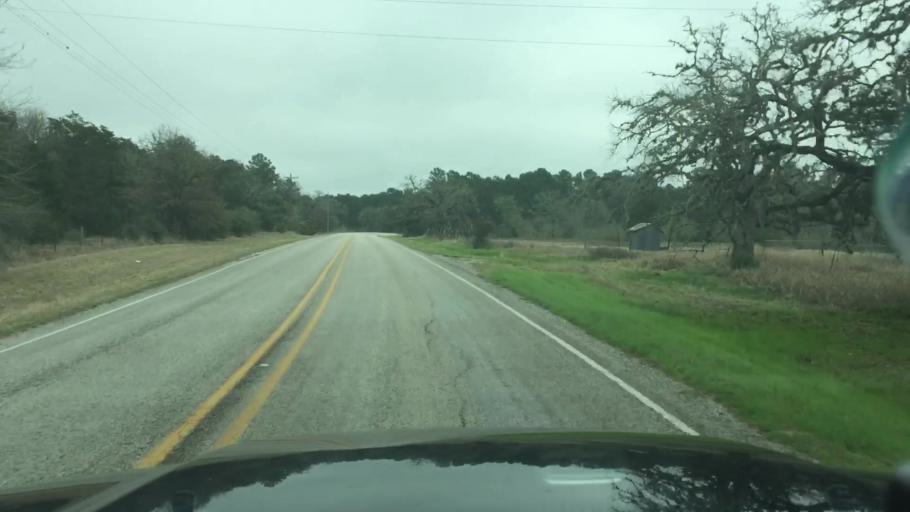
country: US
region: Texas
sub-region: Fayette County
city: La Grange
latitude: 30.0122
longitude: -96.9271
